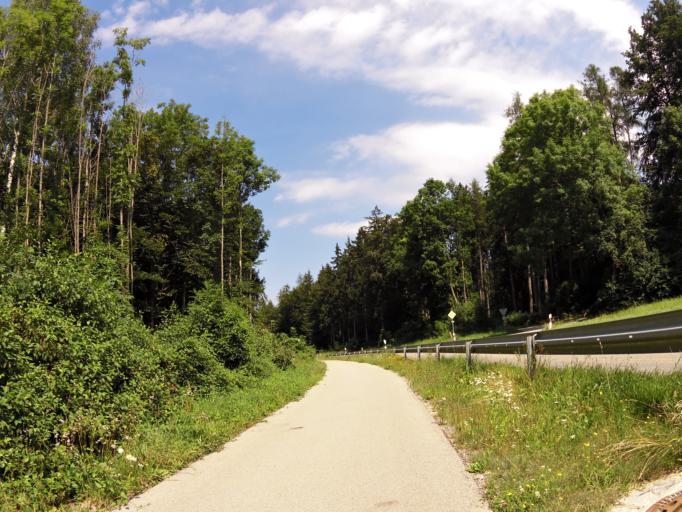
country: DE
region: Bavaria
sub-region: Upper Bavaria
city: Inning am Ammersee
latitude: 48.0586
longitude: 11.1427
